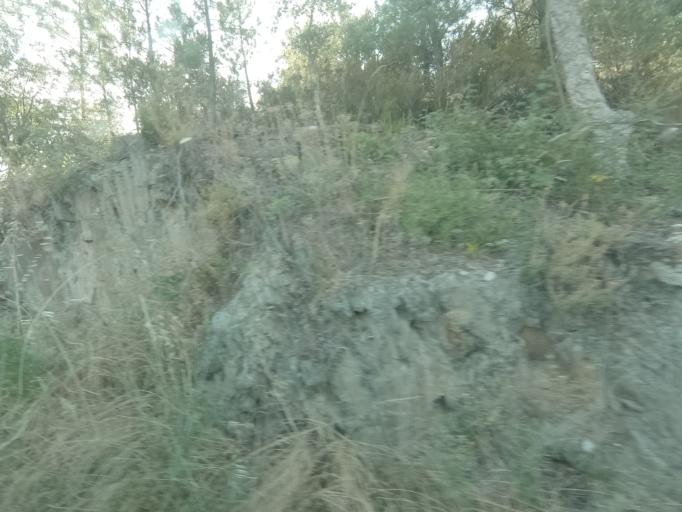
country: PT
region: Vila Real
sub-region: Sabrosa
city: Vilela
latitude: 41.1770
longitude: -7.6043
